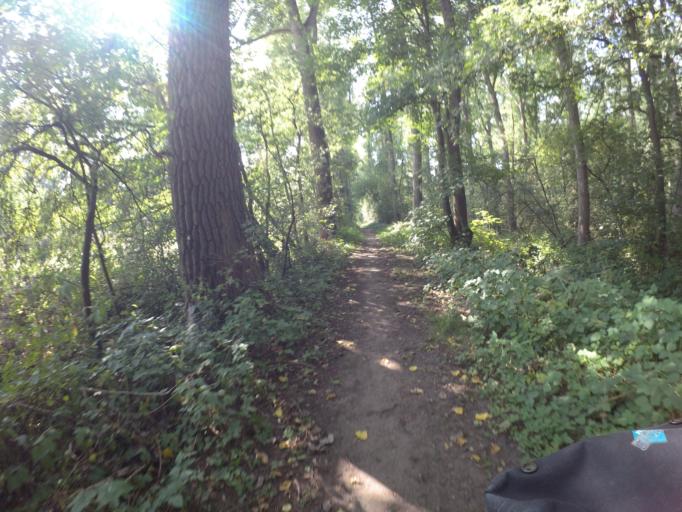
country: NL
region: North Brabant
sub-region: Gemeente Schijndel
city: Schijndel
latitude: 51.6411
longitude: 5.4581
